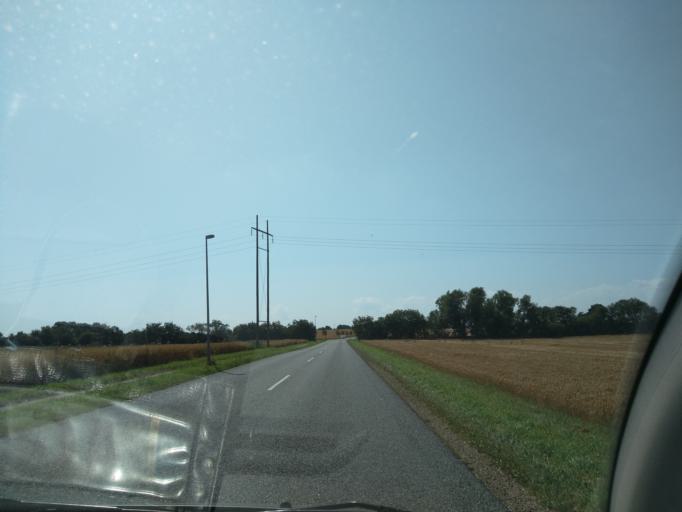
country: DK
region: Central Jutland
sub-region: Viborg Kommune
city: Bjerringbro
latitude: 56.2629
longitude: 9.7173
